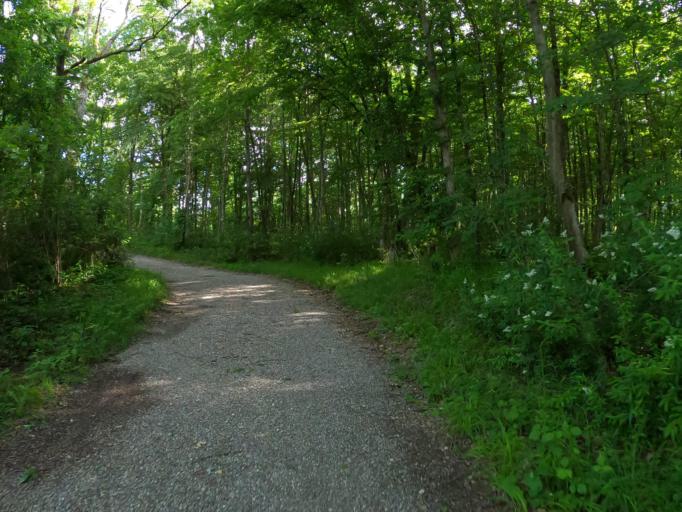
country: DE
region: Bavaria
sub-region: Swabia
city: Nersingen
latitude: 48.4420
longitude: 10.1186
